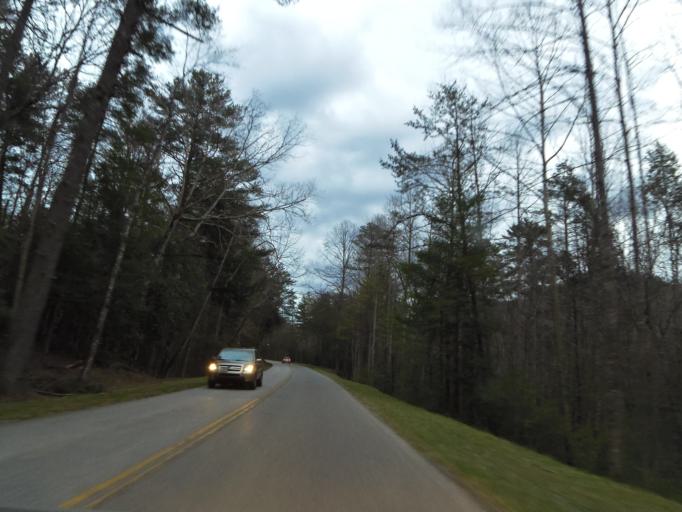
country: US
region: Tennessee
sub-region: Blount County
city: Wildwood
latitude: 35.6049
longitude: -83.7671
